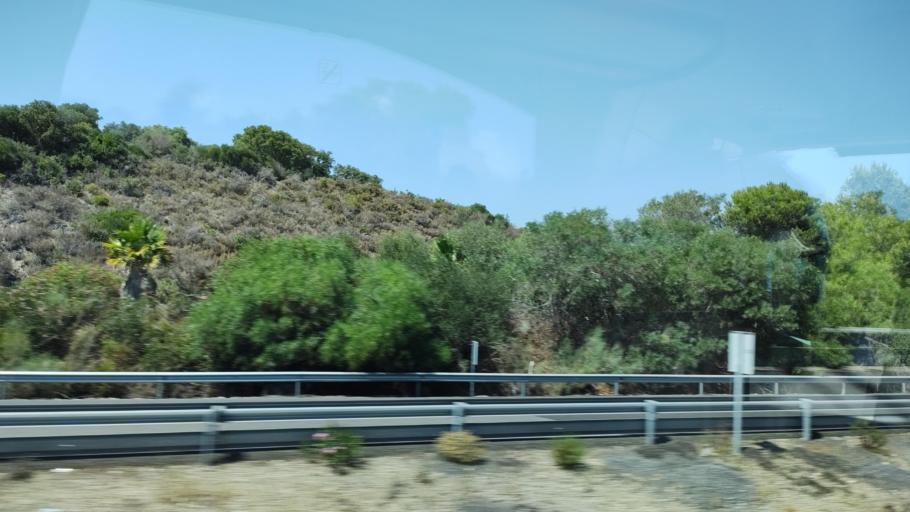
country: ES
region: Andalusia
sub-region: Provincia de Cadiz
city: San Roque
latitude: 36.2631
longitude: -5.3209
